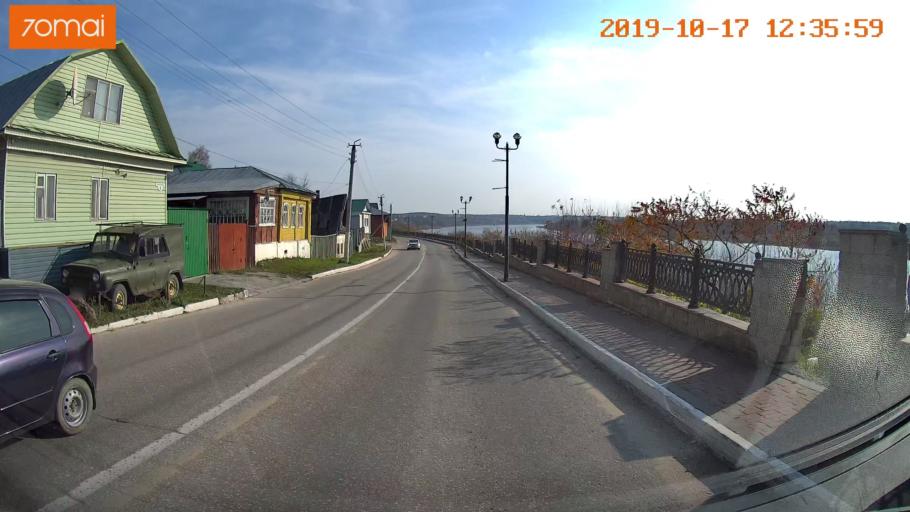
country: RU
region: Rjazan
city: Kasimov
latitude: 54.9412
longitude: 41.3719
